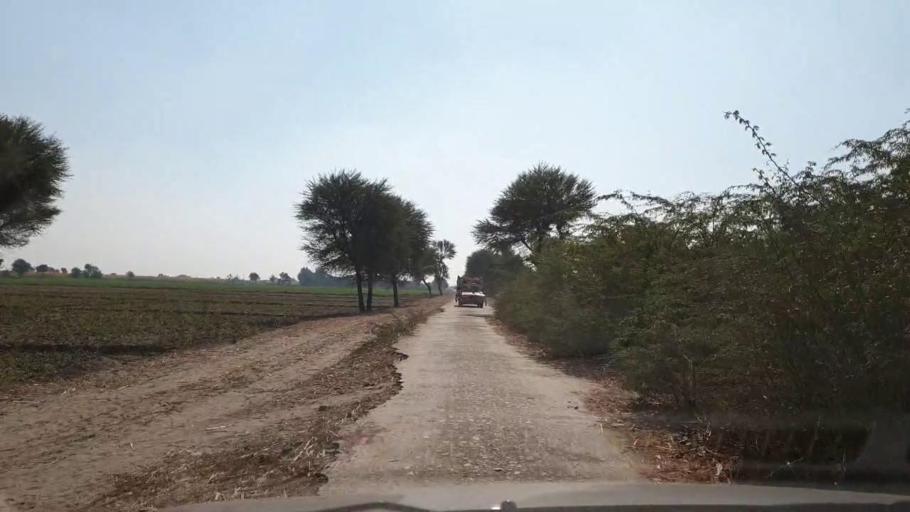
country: PK
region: Sindh
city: Jhol
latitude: 25.8998
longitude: 68.8294
